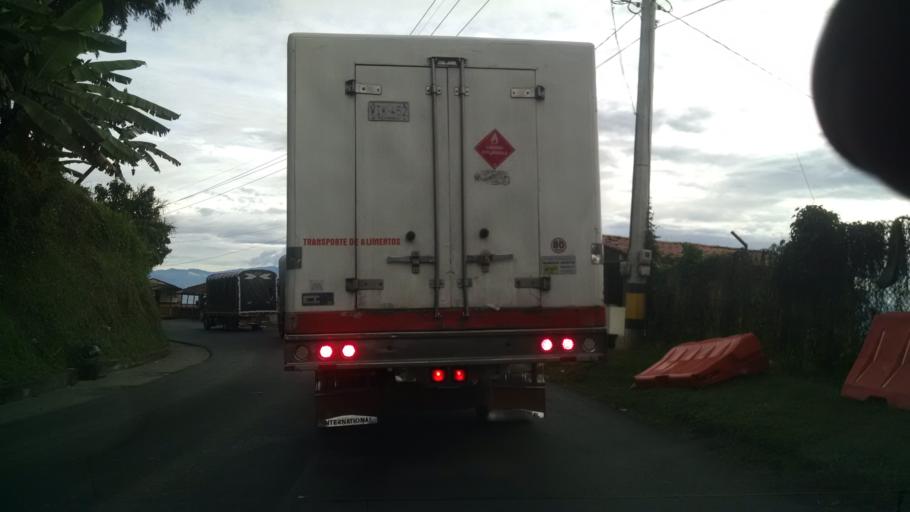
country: CO
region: Antioquia
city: Santa Barbara
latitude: 5.9175
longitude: -75.5789
